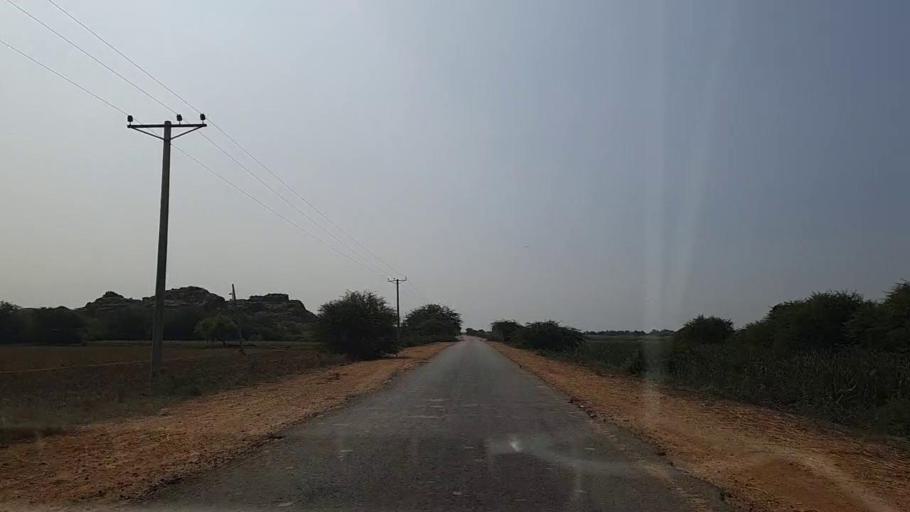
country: PK
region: Sindh
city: Chuhar Jamali
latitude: 24.3642
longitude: 67.9625
